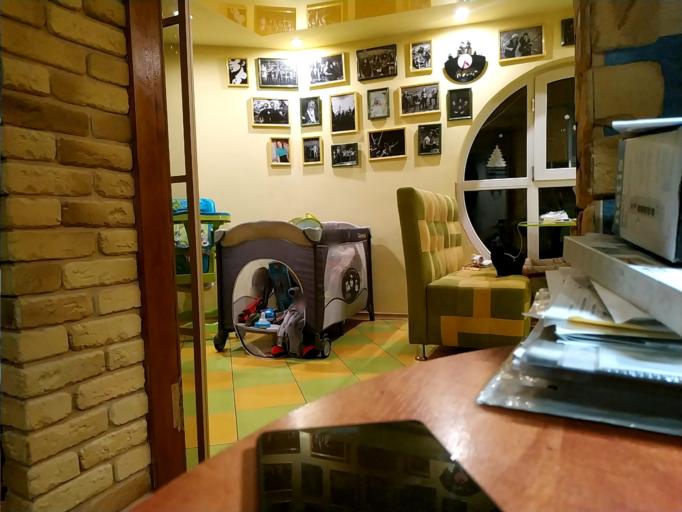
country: RU
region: Orjol
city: Naryshkino
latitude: 53.0375
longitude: 35.6830
